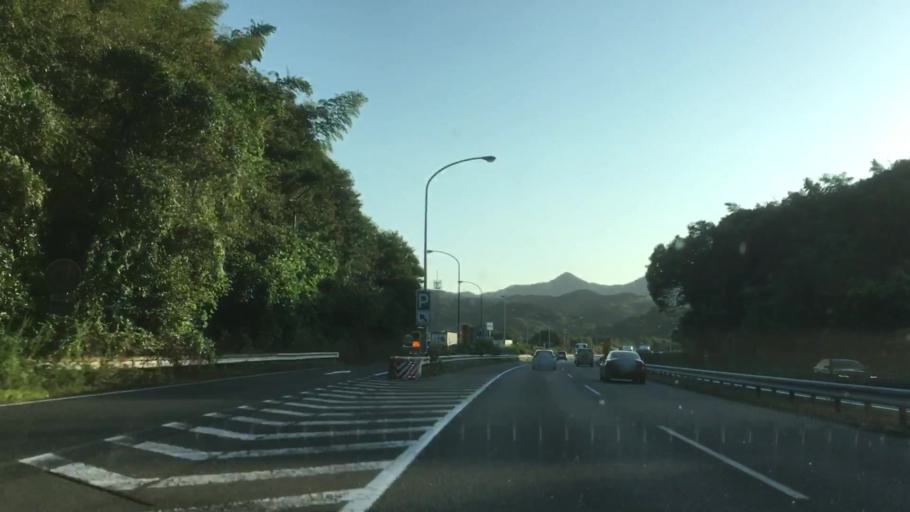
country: JP
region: Yamaguchi
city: Shimonoseki
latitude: 34.0522
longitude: 131.0056
